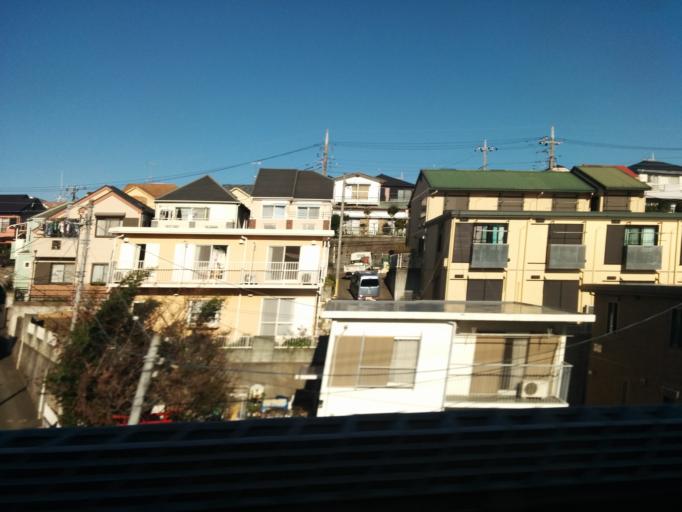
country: JP
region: Kanagawa
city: Minami-rinkan
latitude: 35.4571
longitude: 139.5292
